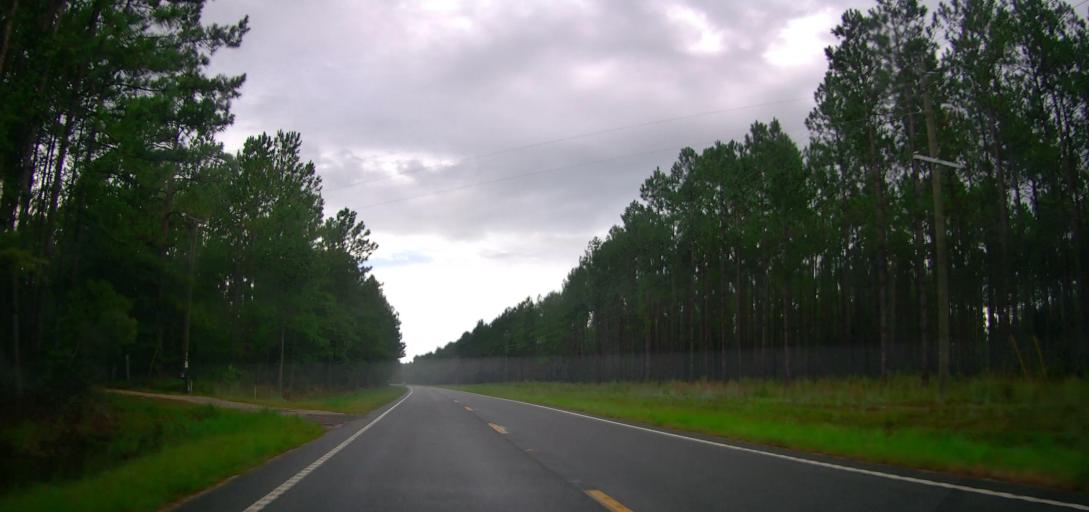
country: US
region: Georgia
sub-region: Ware County
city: Deenwood
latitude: 31.2679
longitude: -82.5218
